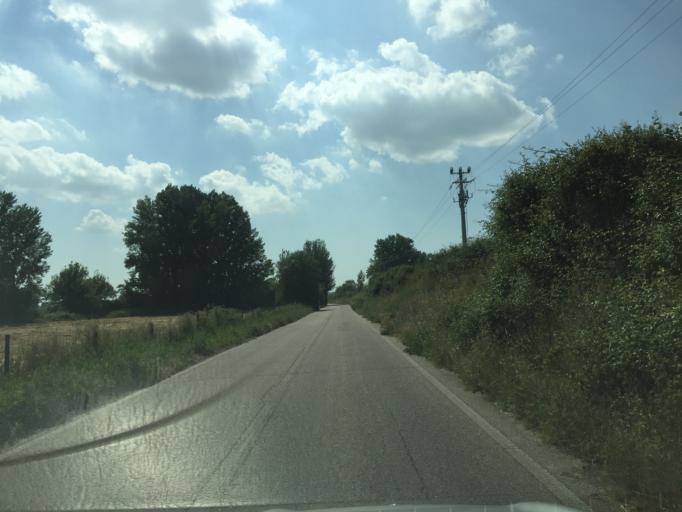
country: PT
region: Santarem
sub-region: Alpiarca
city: Alpiarca
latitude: 39.3035
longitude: -8.5682
